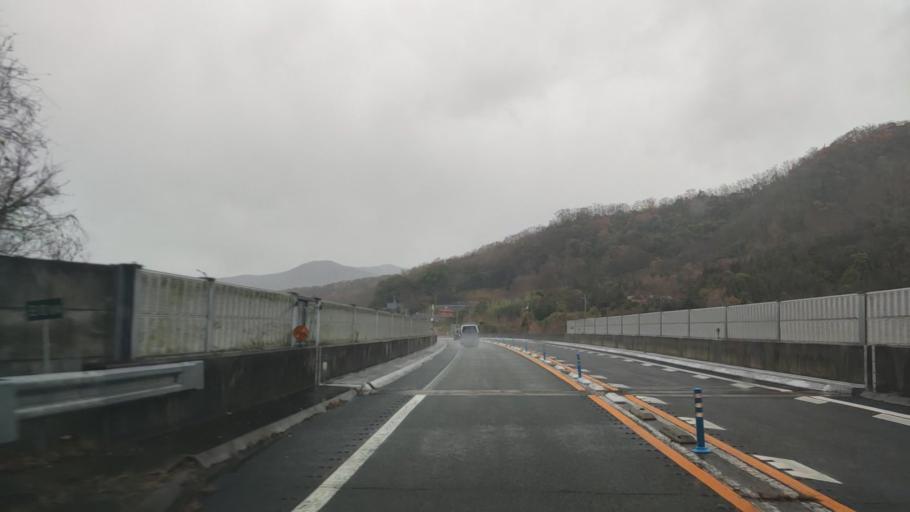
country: JP
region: Tokushima
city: Kamojimacho-jogejima
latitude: 34.1079
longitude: 134.2895
